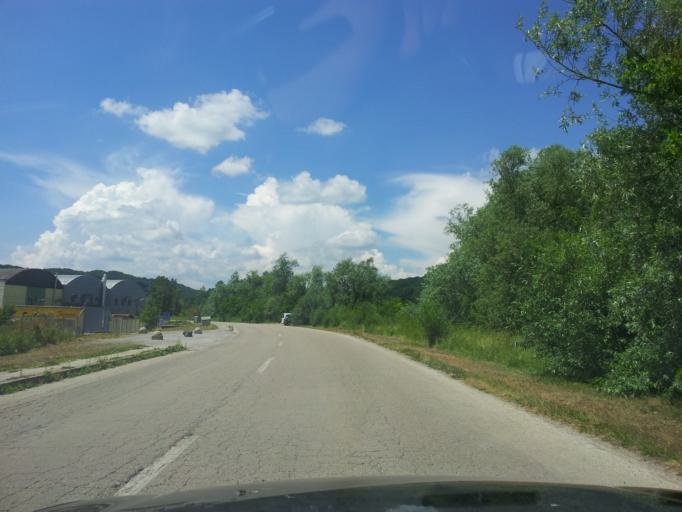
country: HR
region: Karlovacka
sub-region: Grad Karlovac
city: Karlovac
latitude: 45.4639
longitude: 15.5365
